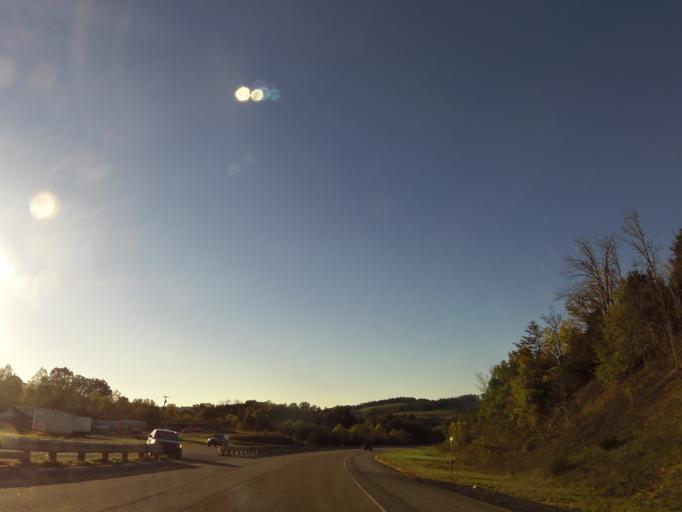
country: US
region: Tennessee
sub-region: Grainger County
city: Rutledge
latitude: 36.3473
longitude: -83.4297
